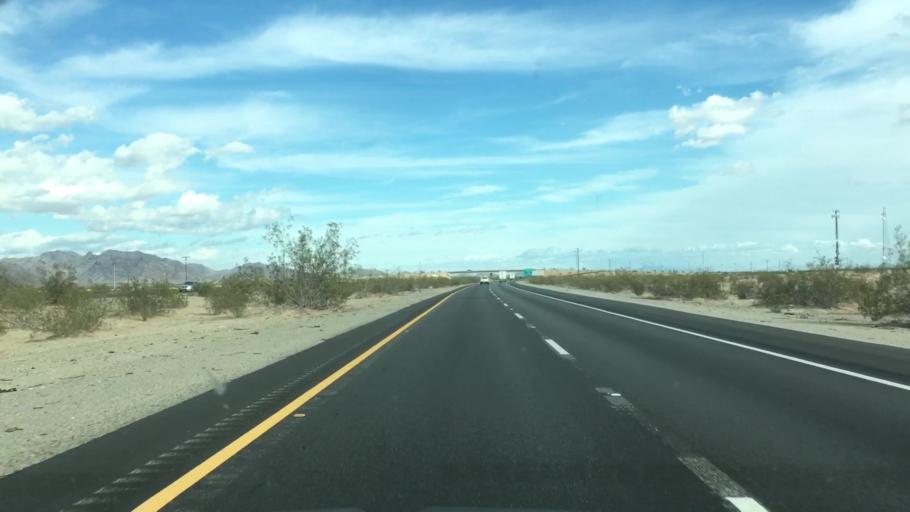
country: US
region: California
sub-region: Riverside County
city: Mesa Verde
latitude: 33.6073
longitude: -114.9097
